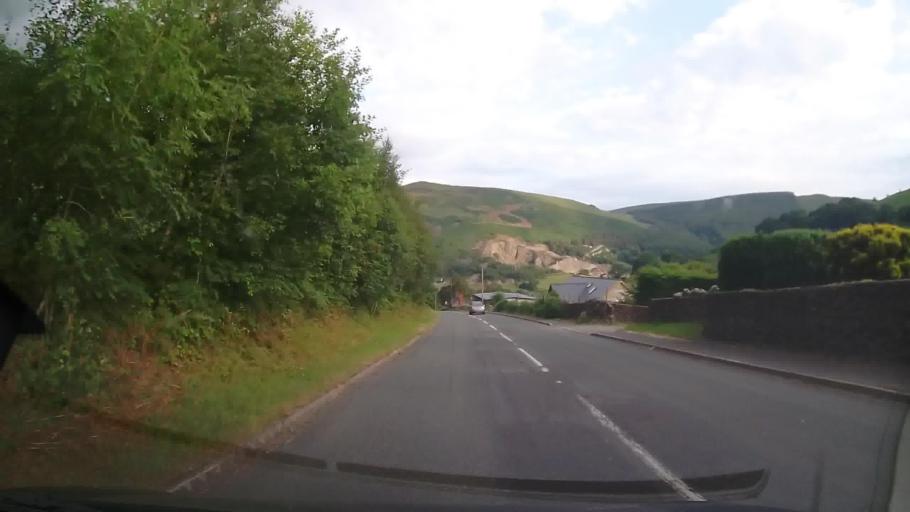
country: GB
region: Wales
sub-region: Sir Powys
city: Llangynog
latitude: 52.8288
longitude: -3.4126
